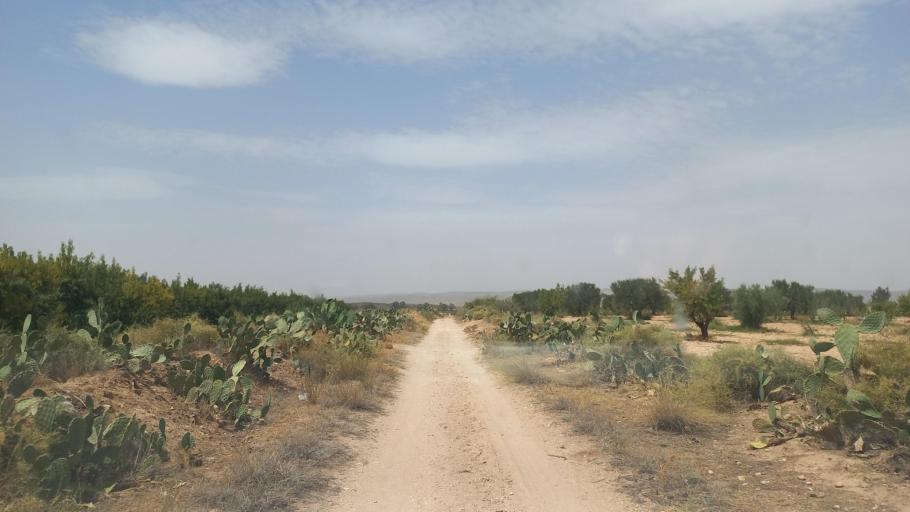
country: TN
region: Al Qasrayn
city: Kasserine
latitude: 35.2618
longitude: 8.9878
